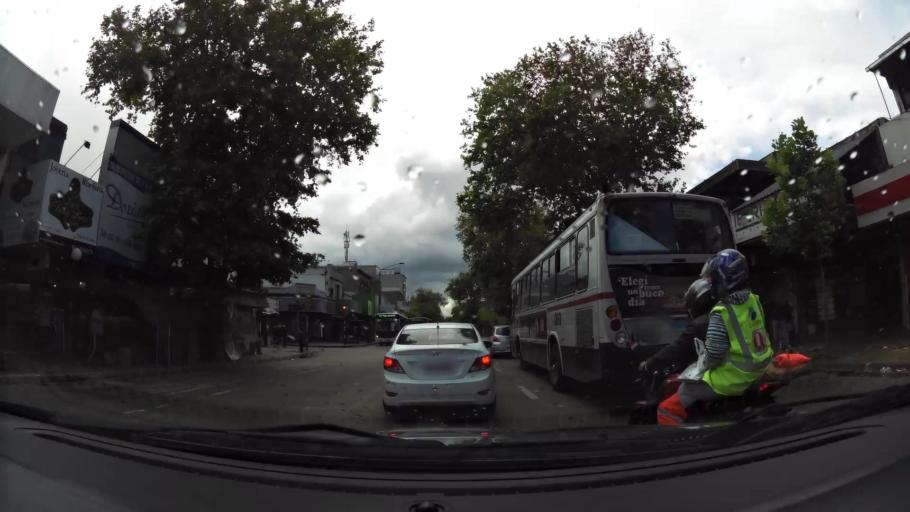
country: UY
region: Montevideo
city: Montevideo
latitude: -34.8753
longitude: -56.1410
